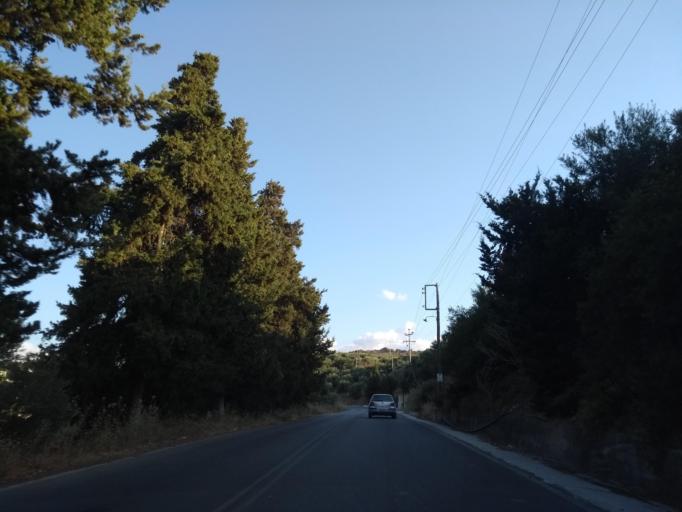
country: GR
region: Crete
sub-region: Nomos Chanias
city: Kalivai
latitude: 35.4372
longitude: 24.1757
